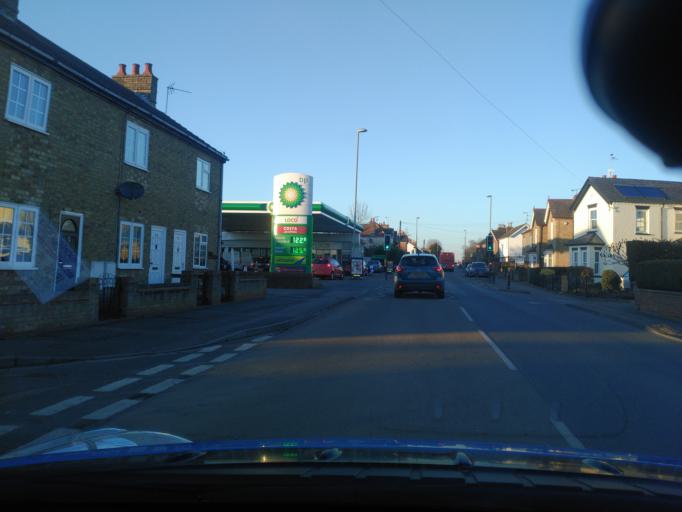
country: GB
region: England
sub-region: Central Bedfordshire
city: Toddington
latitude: 51.9429
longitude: -0.5341
